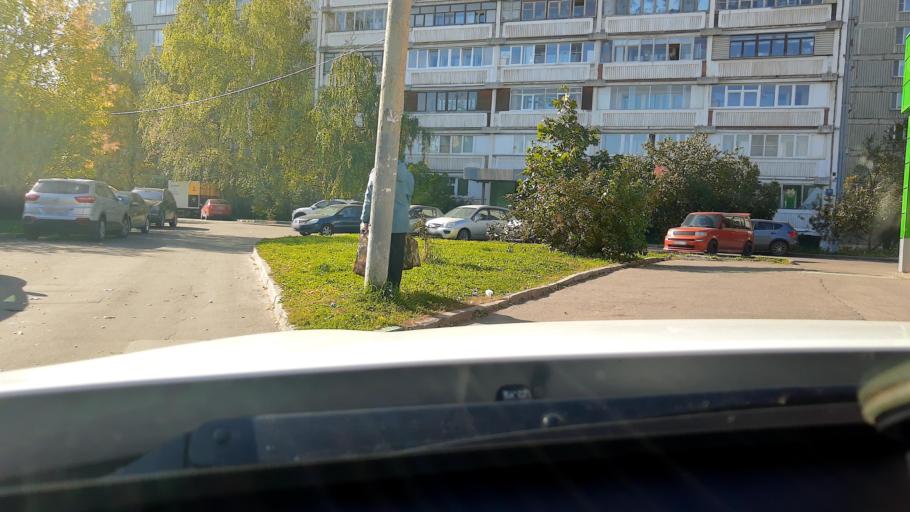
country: RU
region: Moskovskaya
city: Vostochnoe Degunino
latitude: 55.8862
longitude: 37.5641
